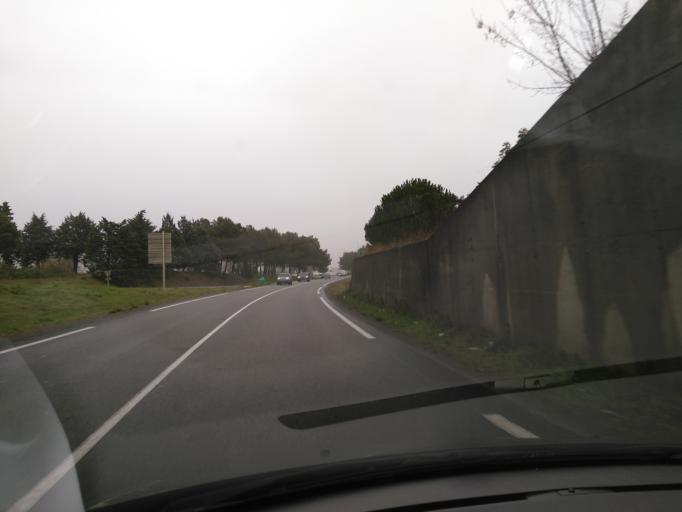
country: FR
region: Languedoc-Roussillon
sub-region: Departement de l'Aude
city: Pennautier
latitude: 43.2123
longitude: 2.3156
